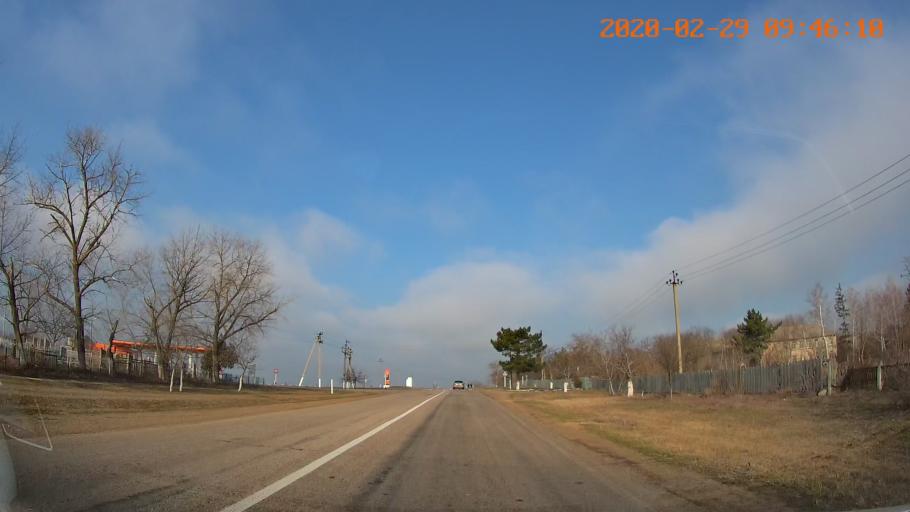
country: MD
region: Telenesti
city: Crasnoe
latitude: 46.6647
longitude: 29.8015
